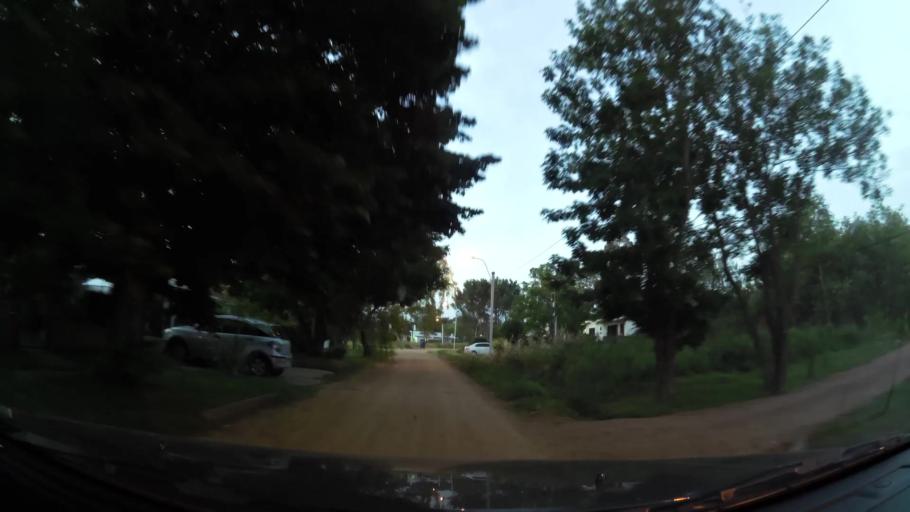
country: UY
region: Canelones
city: Atlantida
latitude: -34.7727
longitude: -55.7494
